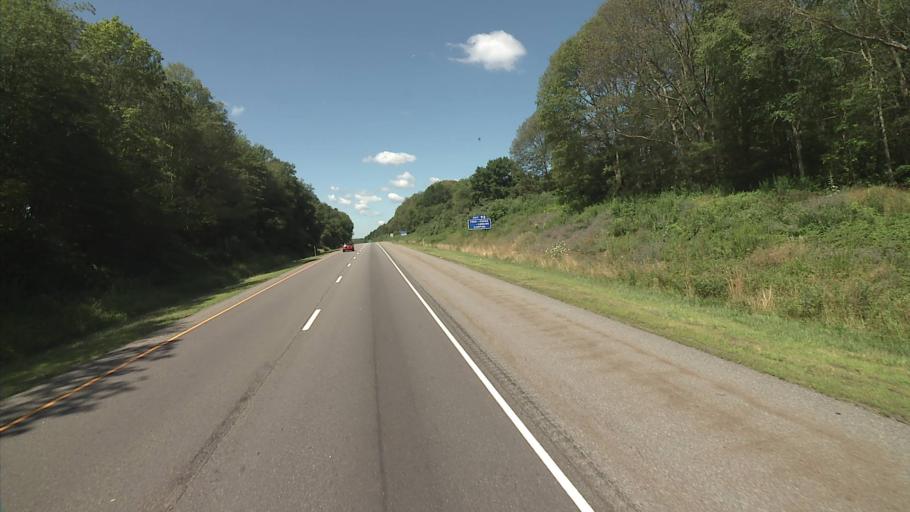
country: US
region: Connecticut
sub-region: New London County
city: Pawcatuck
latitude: 41.4245
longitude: -71.8341
